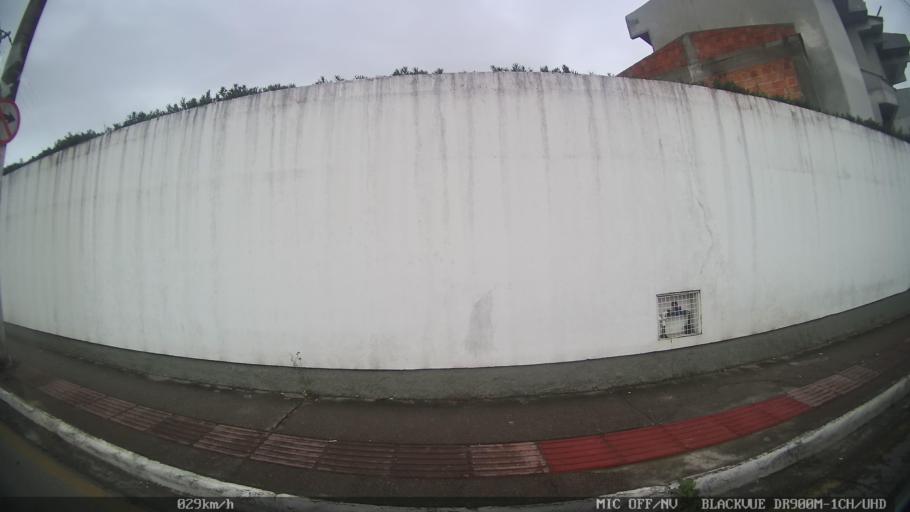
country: BR
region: Santa Catarina
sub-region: Sao Jose
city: Campinas
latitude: -27.5950
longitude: -48.6227
